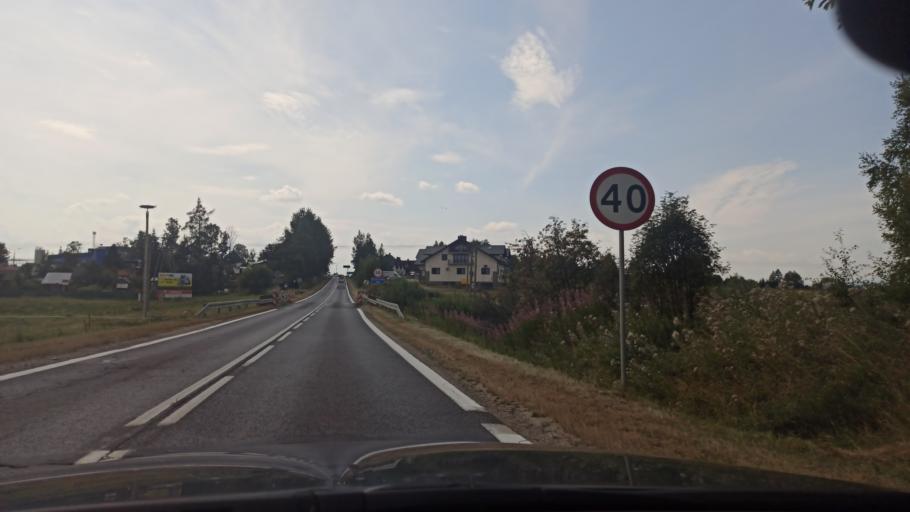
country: PL
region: Lesser Poland Voivodeship
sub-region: Powiat nowotarski
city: Waksmund
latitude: 49.4787
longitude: 20.0570
